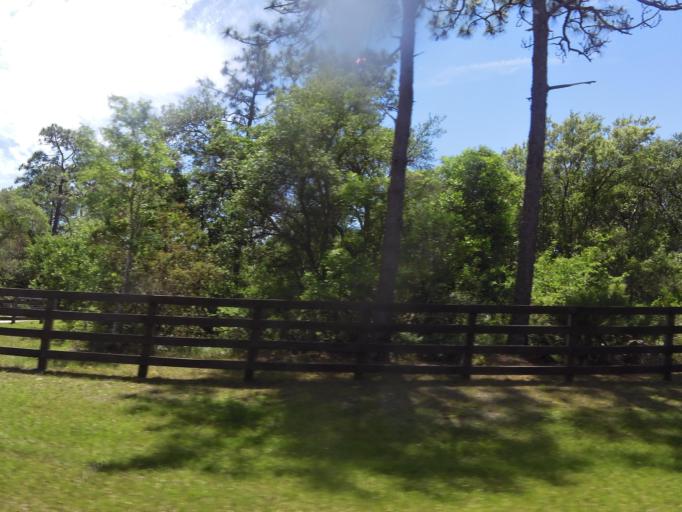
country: US
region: Florida
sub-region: Duval County
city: Atlantic Beach
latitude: 30.4611
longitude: -81.4809
